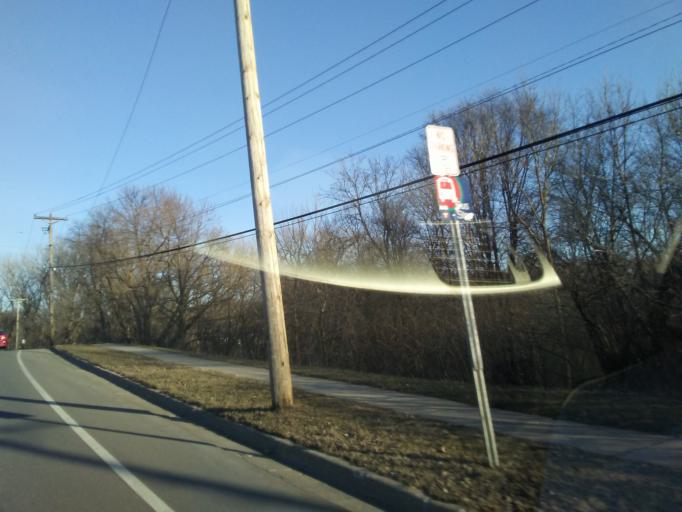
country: US
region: Minnesota
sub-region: Hennepin County
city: Bloomington
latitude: 44.8516
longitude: -93.3260
